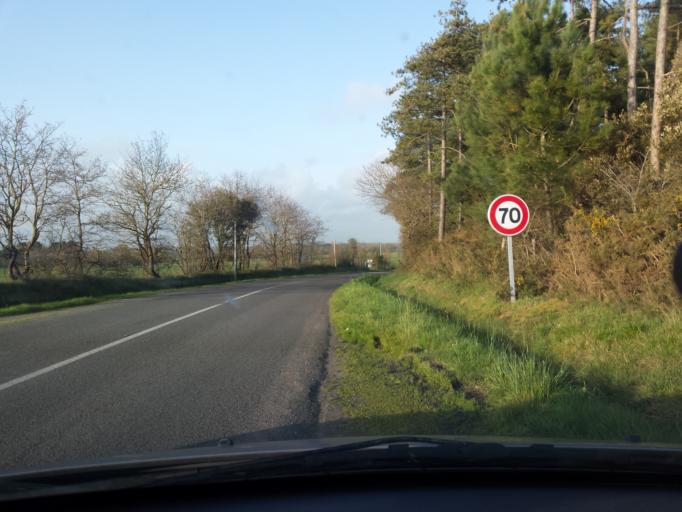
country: FR
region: Pays de la Loire
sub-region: Departement de la Vendee
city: Vaire
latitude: 46.5686
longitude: -1.7652
